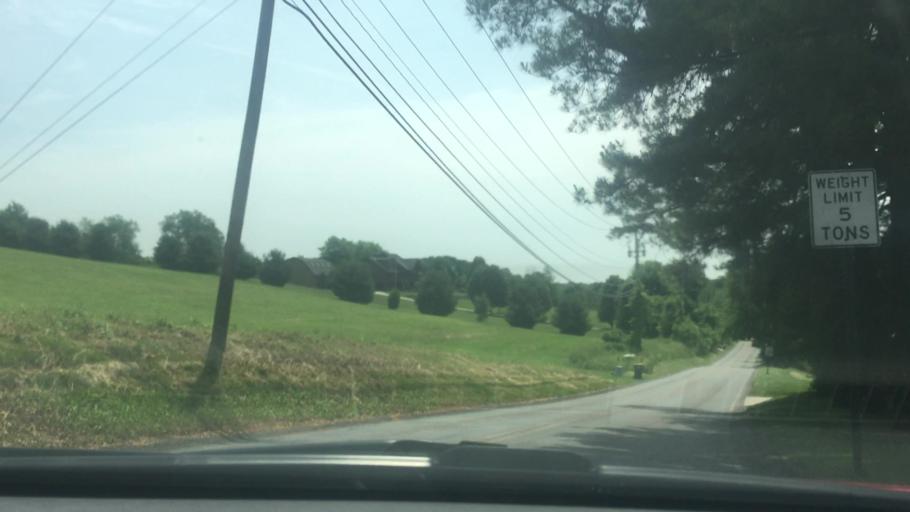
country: US
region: Pennsylvania
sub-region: Allegheny County
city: Bridgeville
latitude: 40.3462
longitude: -80.1500
